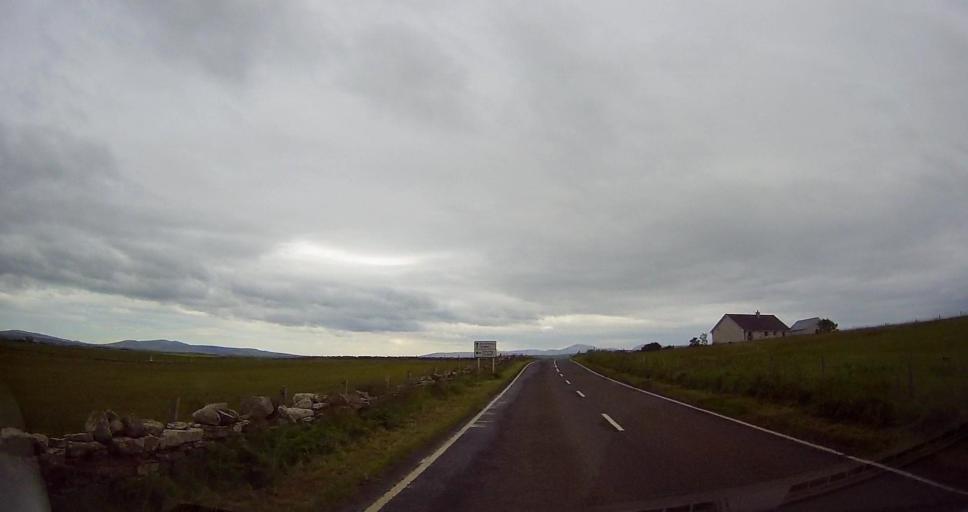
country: GB
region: Scotland
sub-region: Orkney Islands
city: Stromness
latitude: 59.0765
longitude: -3.2779
